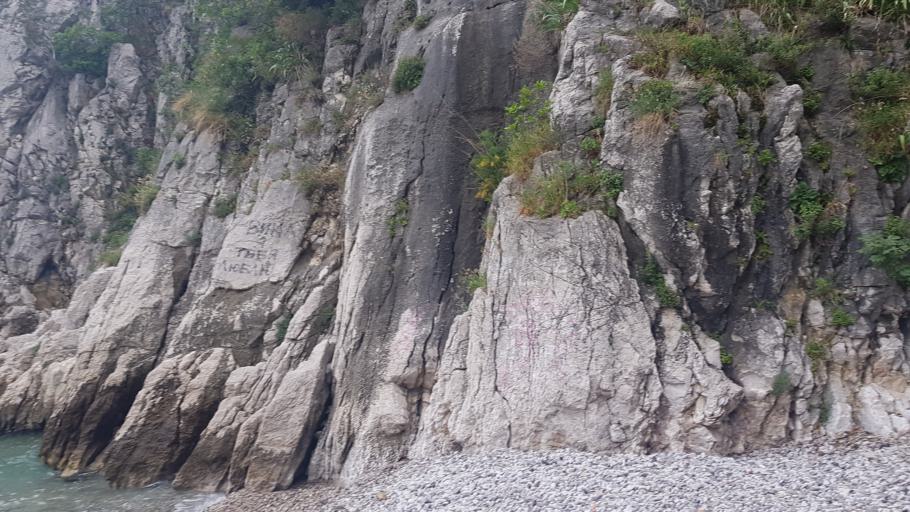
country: IT
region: Friuli Venezia Giulia
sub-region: Provincia di Trieste
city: Duino
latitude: 45.7717
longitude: 13.6047
